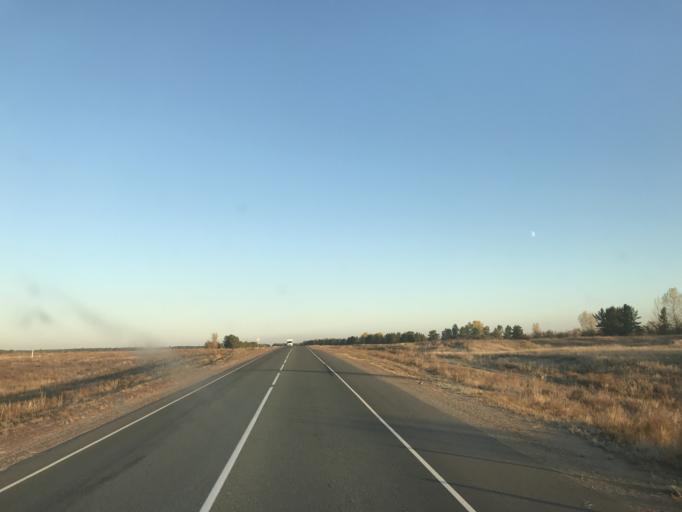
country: KZ
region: East Kazakhstan
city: Semey
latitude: 50.7579
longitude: 79.5978
